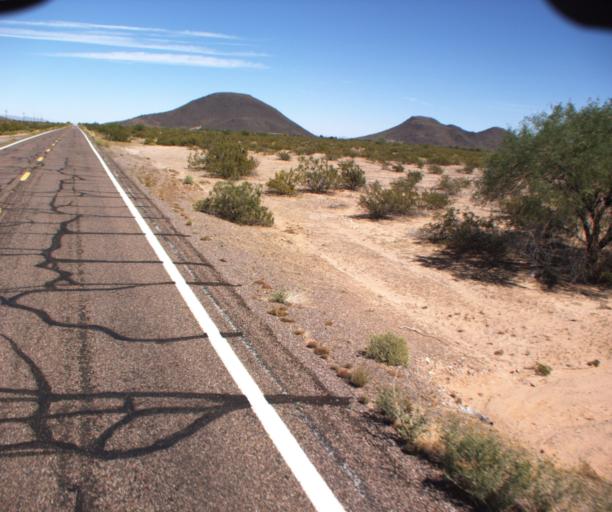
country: US
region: Arizona
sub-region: Maricopa County
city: Gila Bend
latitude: 32.7283
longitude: -112.8363
